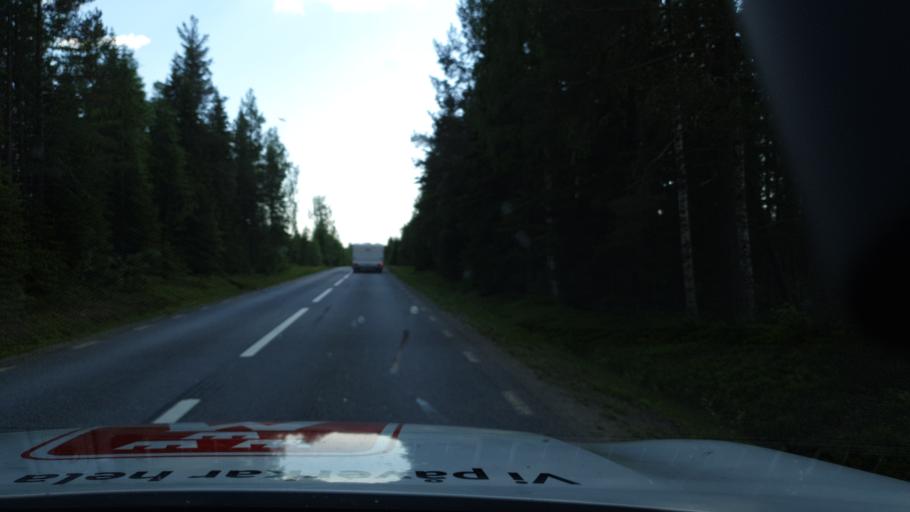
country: SE
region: Vaesterbotten
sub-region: Skelleftea Kommun
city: Burtraesk
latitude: 64.3746
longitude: 20.2507
